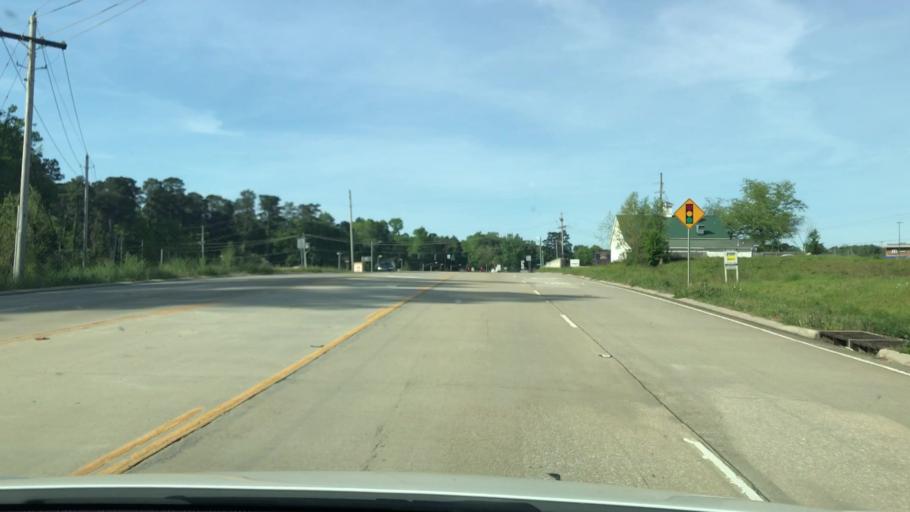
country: US
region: Louisiana
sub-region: Bossier Parish
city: Bossier City
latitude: 32.3961
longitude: -93.7242
